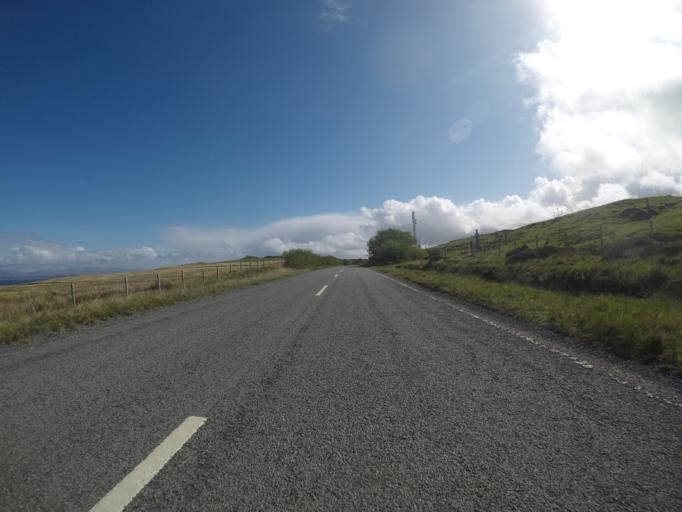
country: GB
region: Scotland
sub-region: Highland
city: Portree
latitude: 57.5896
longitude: -6.1580
